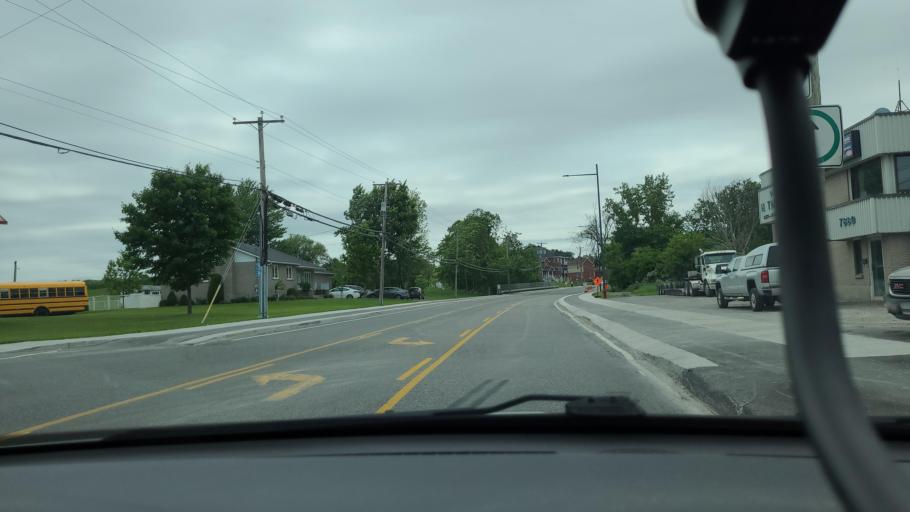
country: CA
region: Quebec
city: Bois-des-Filion
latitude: 45.6514
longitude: -73.7484
